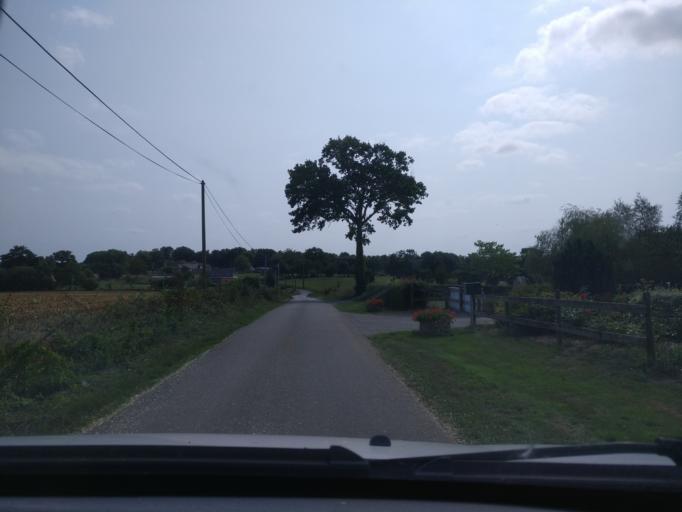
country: FR
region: Brittany
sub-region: Departement d'Ille-et-Vilaine
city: Erce-pres-Liffre
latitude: 48.2659
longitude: -1.5275
